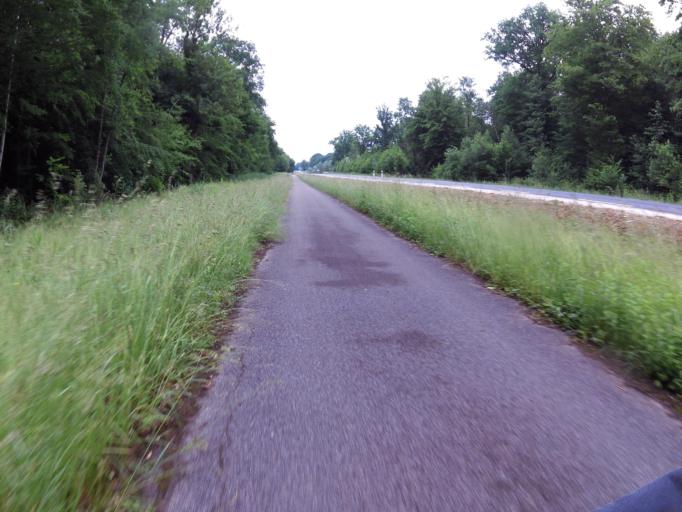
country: FR
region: Champagne-Ardenne
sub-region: Departement de la Haute-Marne
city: Laneuville-a-Remy
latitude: 48.5650
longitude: 4.8445
